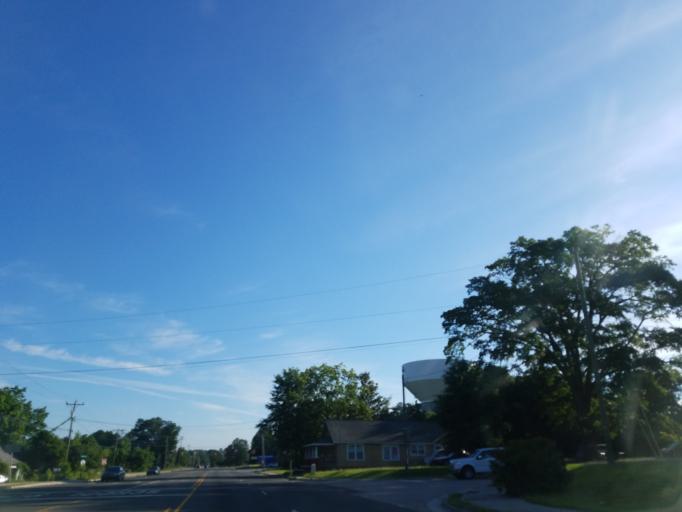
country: US
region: North Carolina
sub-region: Durham County
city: Durham
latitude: 35.9437
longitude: -78.8382
